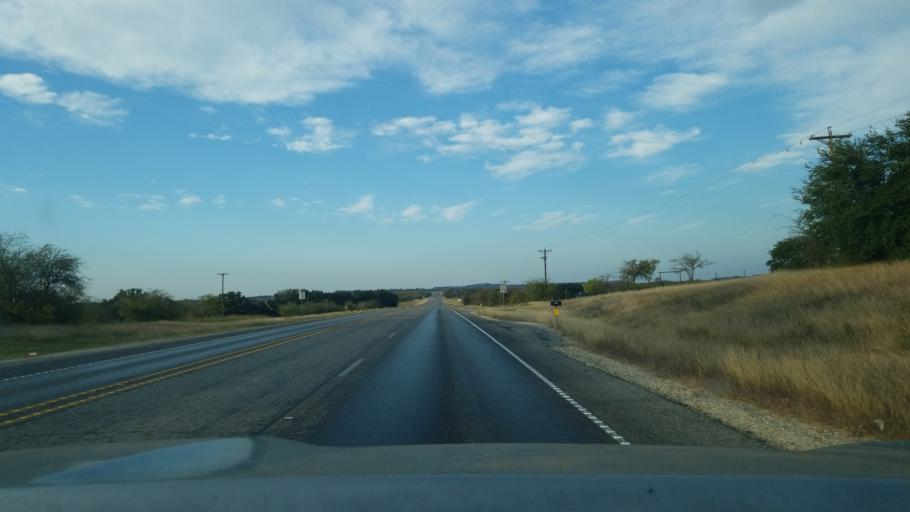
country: US
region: Texas
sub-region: Brown County
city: Lake Brownwood
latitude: 31.9911
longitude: -98.9208
